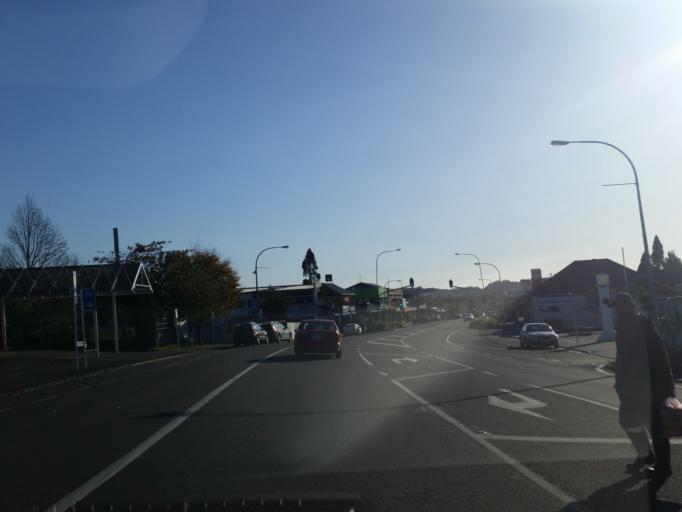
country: NZ
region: Bay of Plenty
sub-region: Western Bay of Plenty District
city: Katikati
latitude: -37.5541
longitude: 175.9171
